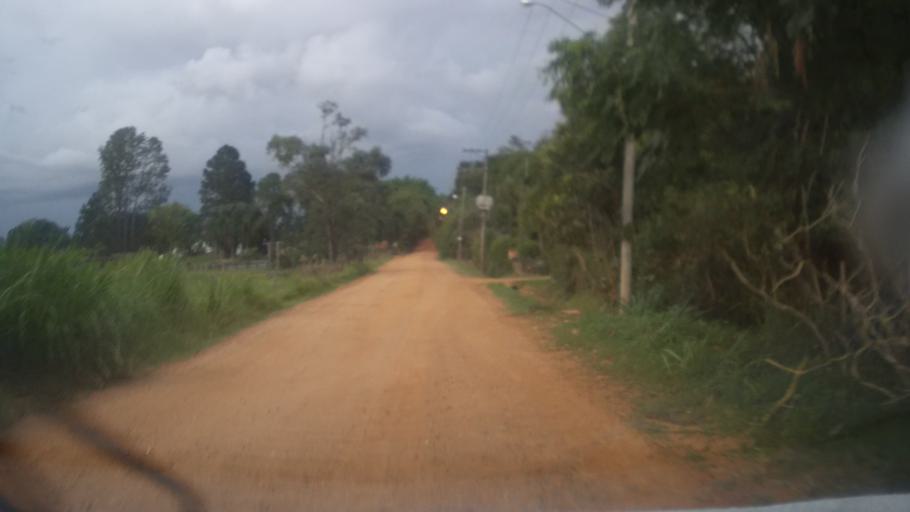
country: BR
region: Sao Paulo
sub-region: Itupeva
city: Itupeva
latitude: -23.1934
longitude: -47.0087
